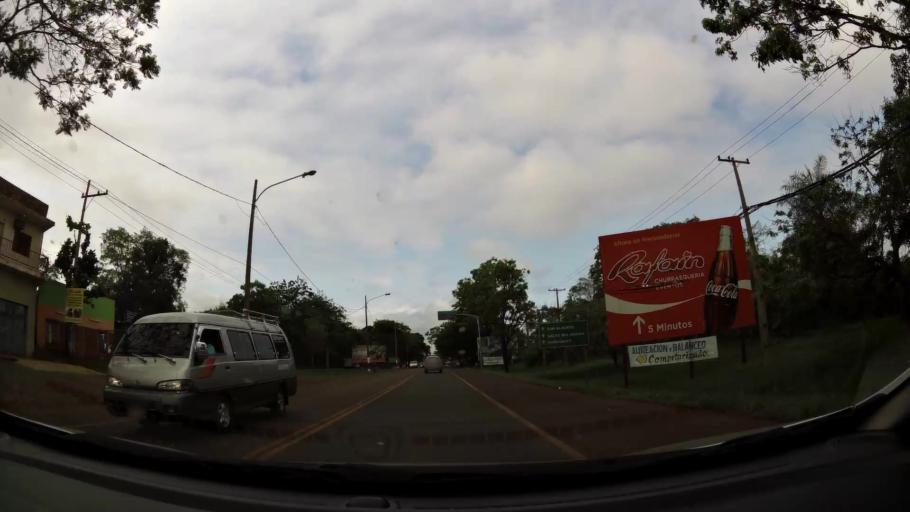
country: PY
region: Alto Parana
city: Ciudad del Este
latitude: -25.4098
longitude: -54.6324
